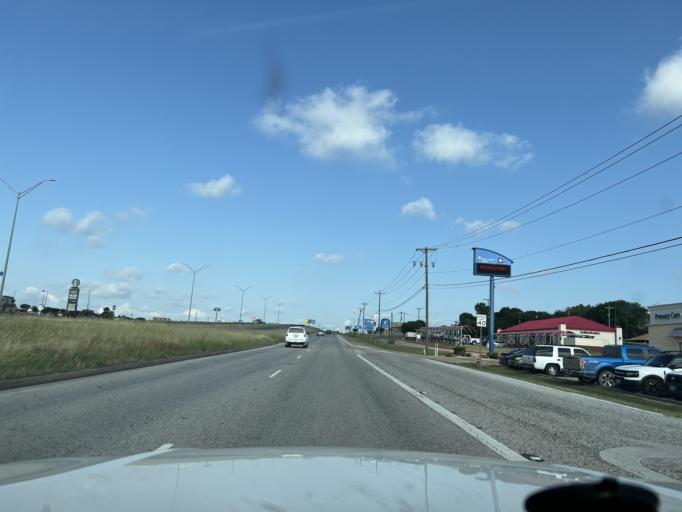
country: US
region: Texas
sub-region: Washington County
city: Brenham
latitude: 30.1429
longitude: -96.3906
